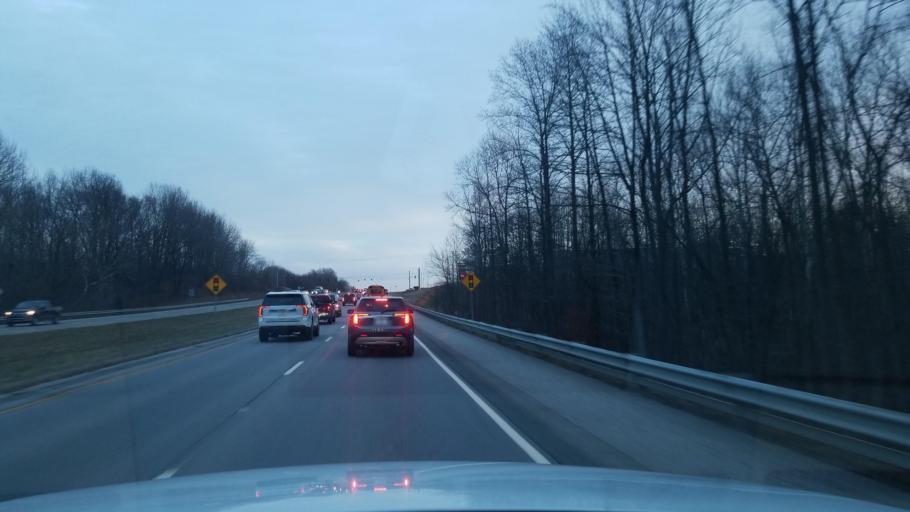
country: US
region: Indiana
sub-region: Vanderburgh County
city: Evansville
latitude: 37.9735
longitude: -87.6498
